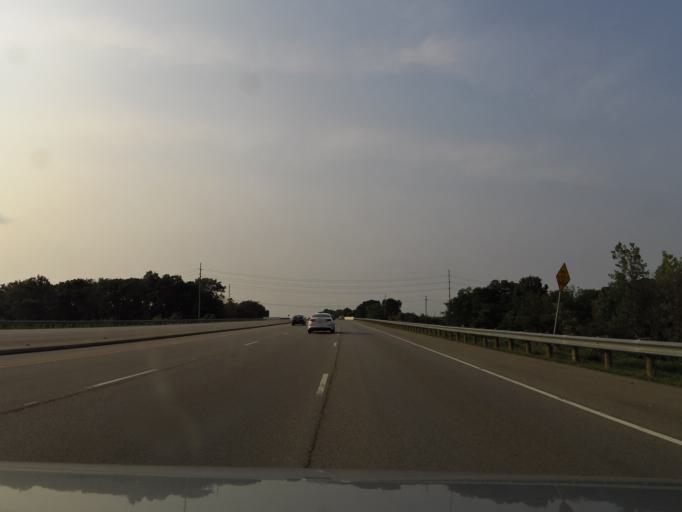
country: US
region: Ohio
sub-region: Hamilton County
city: Forest Park
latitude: 39.3488
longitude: -84.5018
